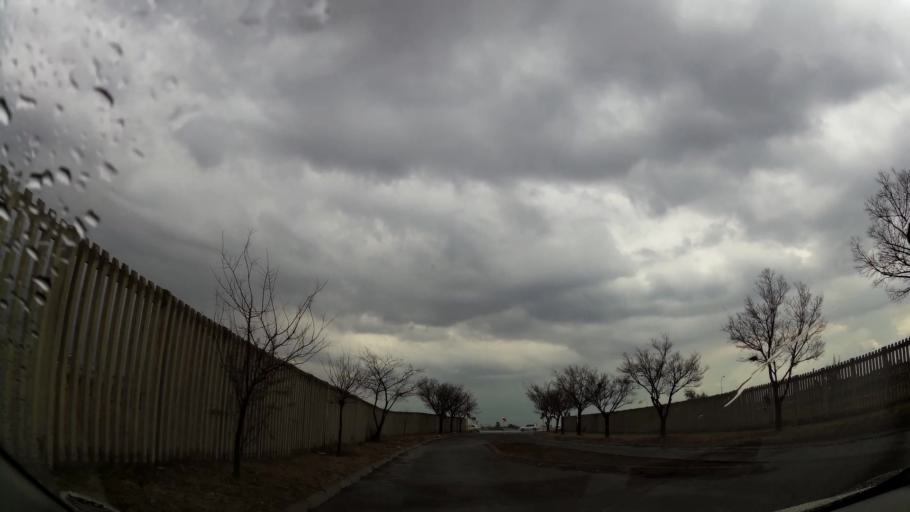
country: ZA
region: Gauteng
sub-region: Ekurhuleni Metropolitan Municipality
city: Germiston
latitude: -26.3788
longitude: 28.1399
